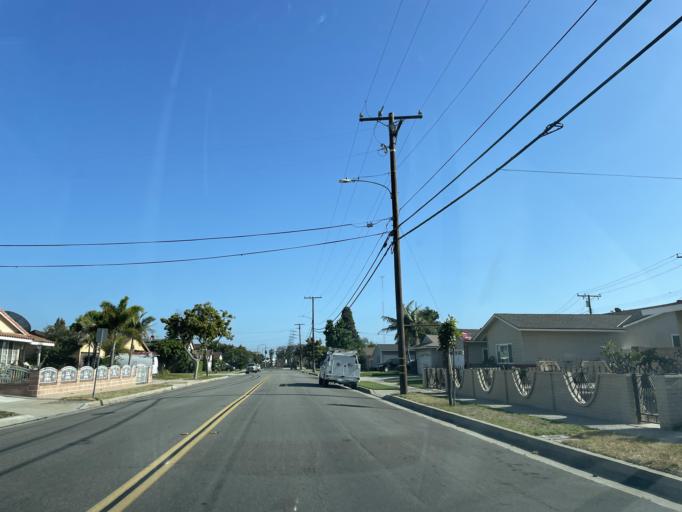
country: US
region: California
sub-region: Orange County
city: Buena Park
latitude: 33.8903
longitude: -118.0116
